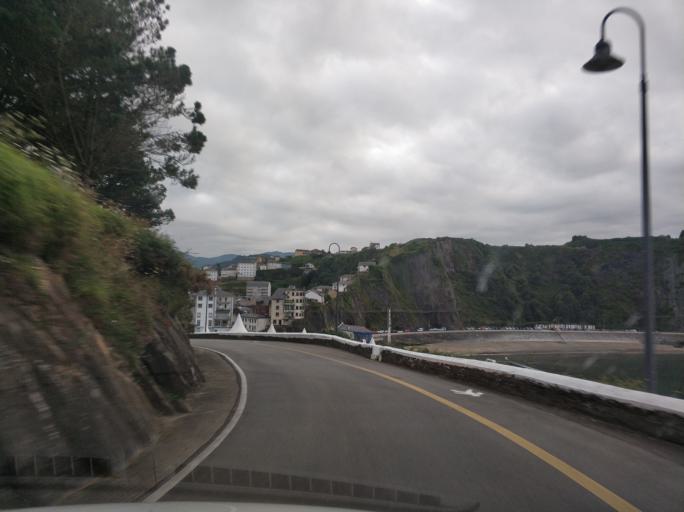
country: ES
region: Asturias
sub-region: Province of Asturias
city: Navia
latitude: 43.5478
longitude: -6.5338
